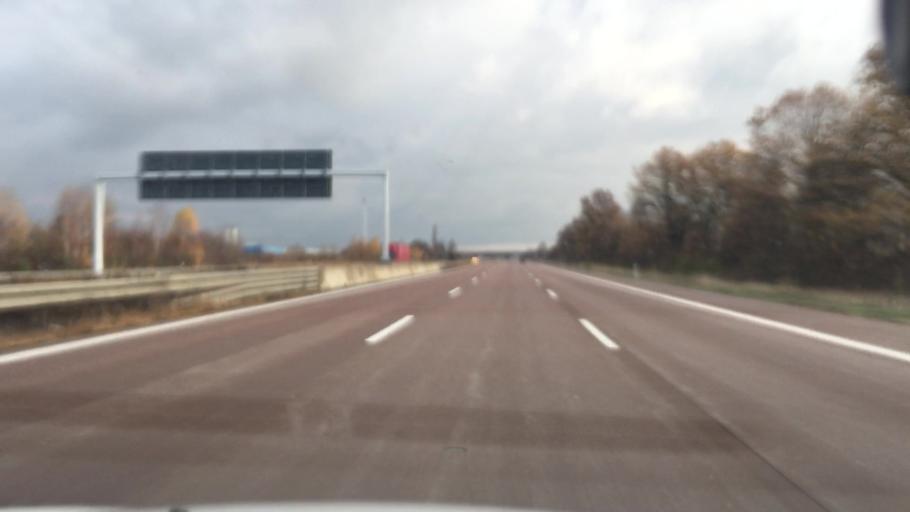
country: DE
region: Saxony-Anhalt
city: Dolbau
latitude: 51.4737
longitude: 12.0829
